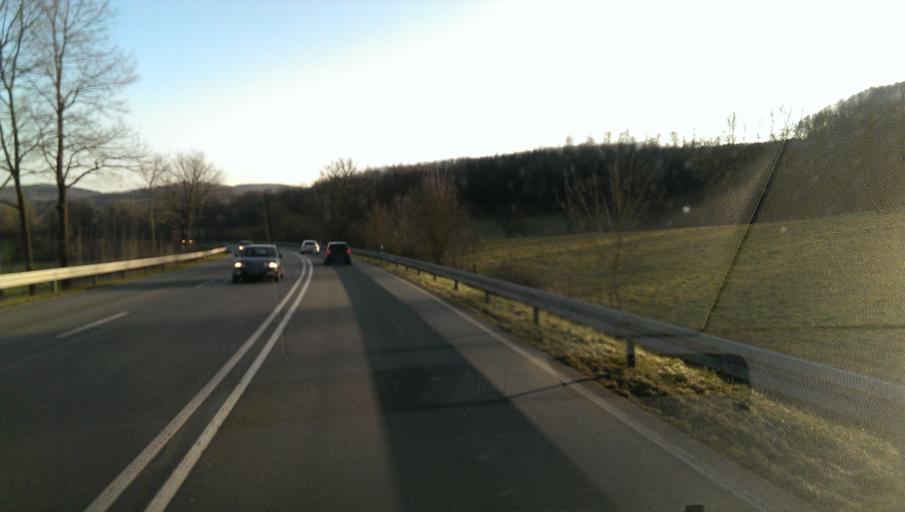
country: DE
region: North Rhine-Westphalia
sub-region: Regierungsbezirk Detmold
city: Bad Driburg
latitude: 51.7216
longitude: 9.0032
